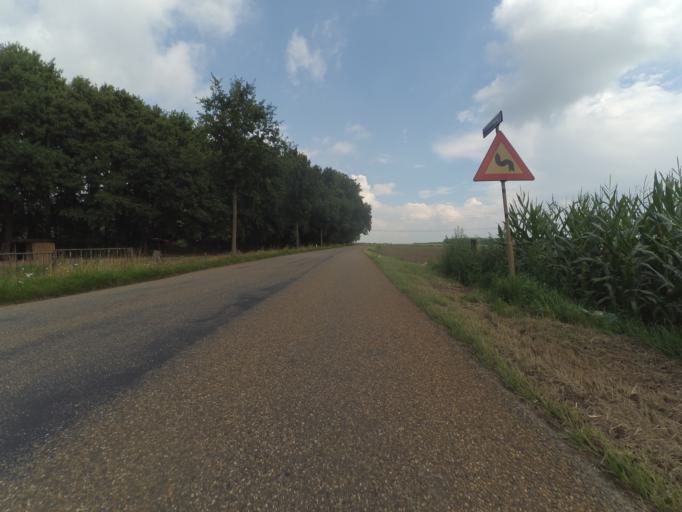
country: NL
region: Limburg
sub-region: Gemeente Roerdalen
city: Montfort
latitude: 51.1391
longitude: 5.9495
